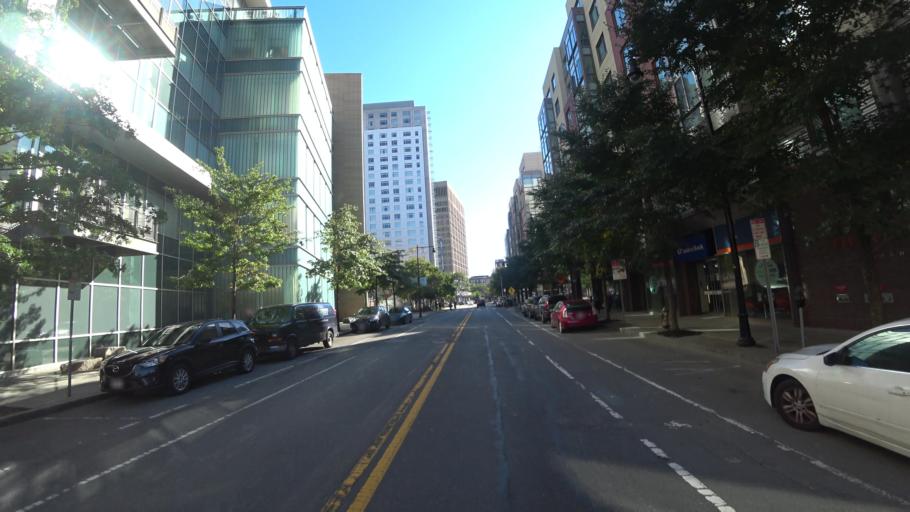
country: US
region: Massachusetts
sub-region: Suffolk County
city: Boston
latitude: 42.3650
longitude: -71.0829
